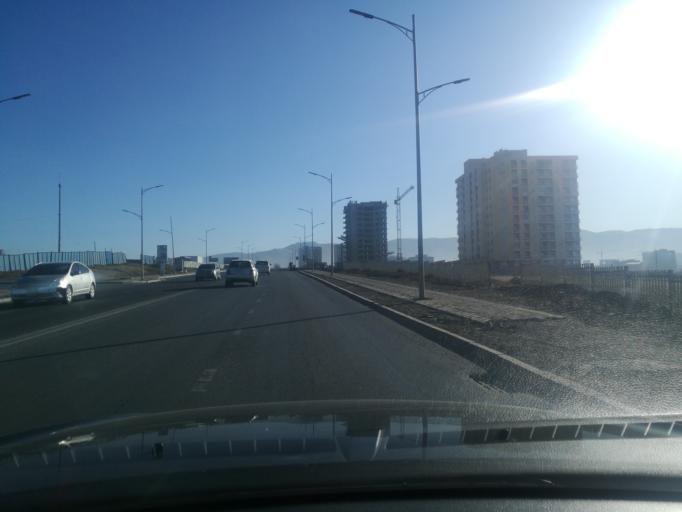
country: MN
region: Ulaanbaatar
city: Ulaanbaatar
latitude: 47.8561
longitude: 106.7692
